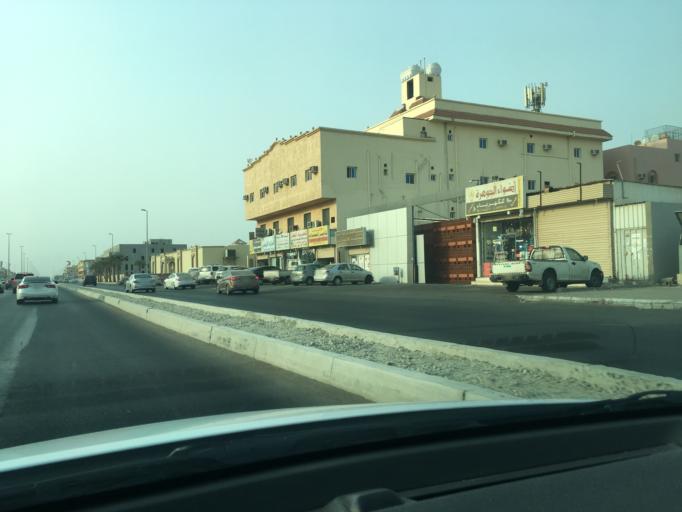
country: SA
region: Makkah
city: Jeddah
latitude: 21.7508
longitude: 39.1878
